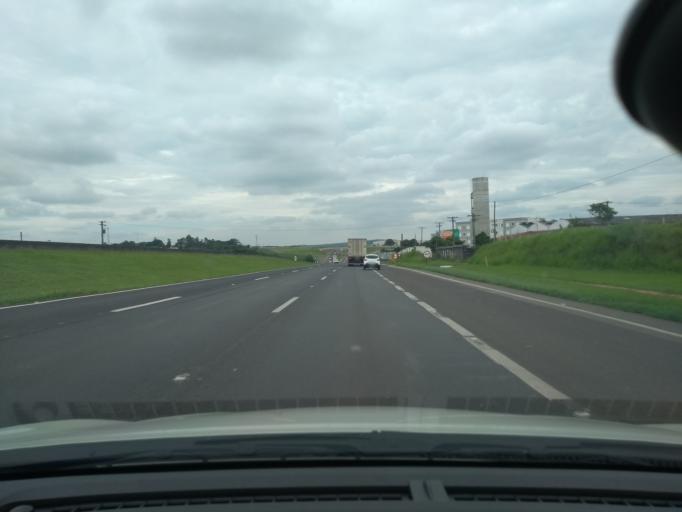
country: BR
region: Sao Paulo
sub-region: Araras
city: Araras
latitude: -22.3857
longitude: -47.3942
